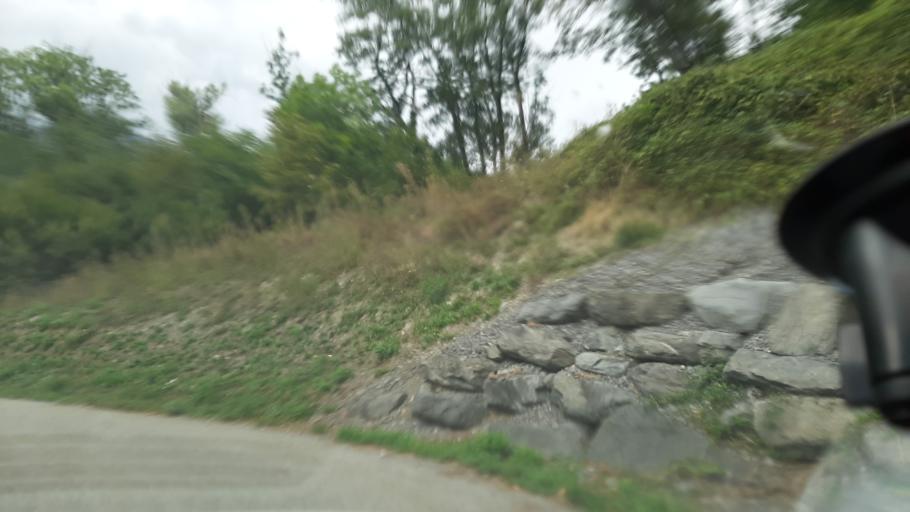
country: FR
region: Rhone-Alpes
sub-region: Departement de la Savoie
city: Saint-Michel-de-Maurienne
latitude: 45.2306
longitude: 6.4622
